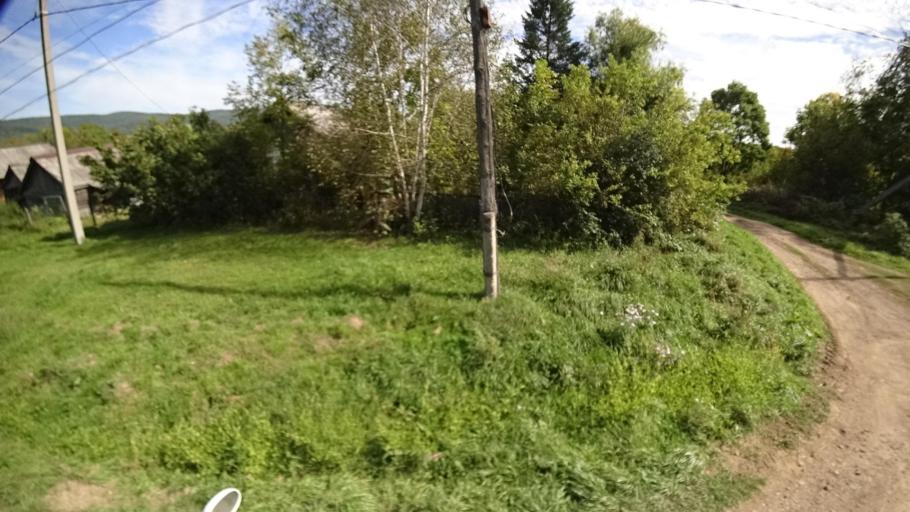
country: RU
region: Primorskiy
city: Yakovlevka
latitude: 44.3967
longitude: 133.5998
